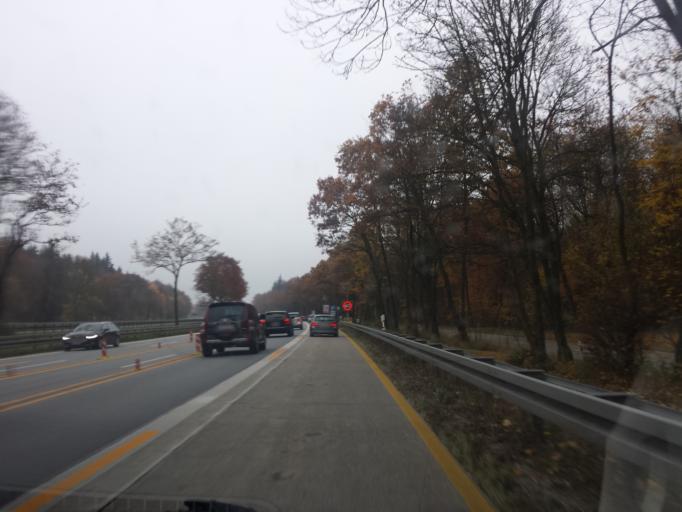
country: DE
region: Bavaria
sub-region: Upper Bavaria
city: Schaftlarn
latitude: 48.0372
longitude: 11.4315
